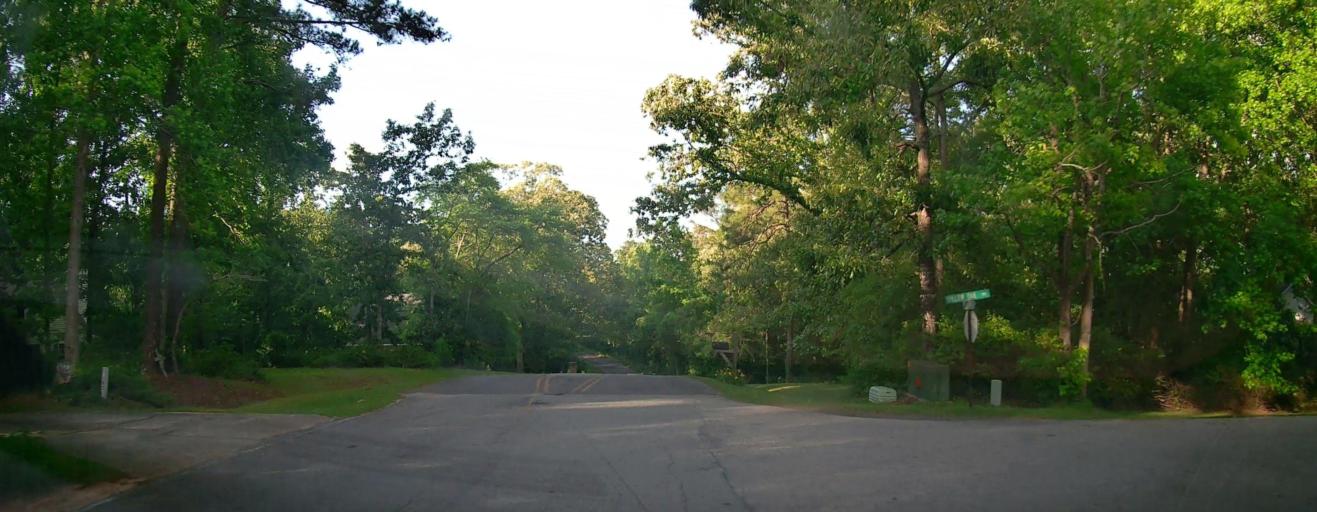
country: US
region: Georgia
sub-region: Peach County
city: Byron
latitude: 32.6352
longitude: -83.7493
